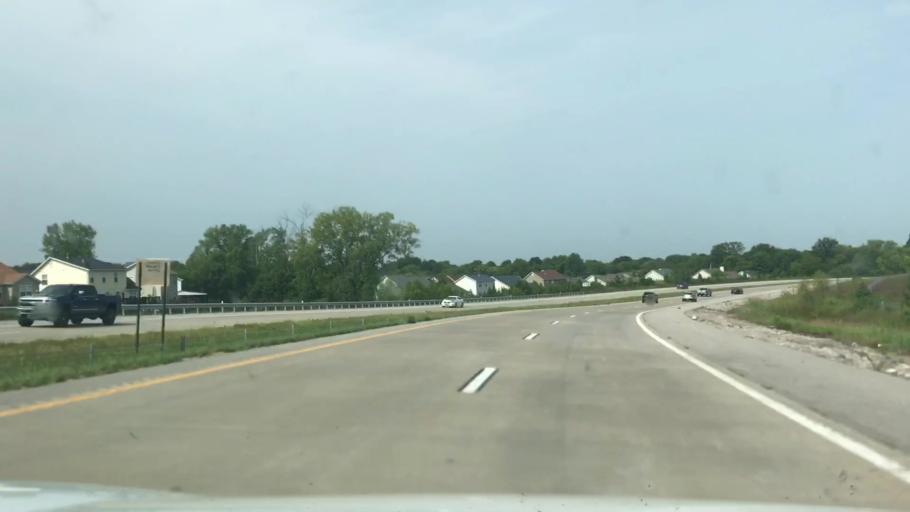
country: US
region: Missouri
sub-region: Saint Charles County
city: Cottleville
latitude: 38.7321
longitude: -90.6601
